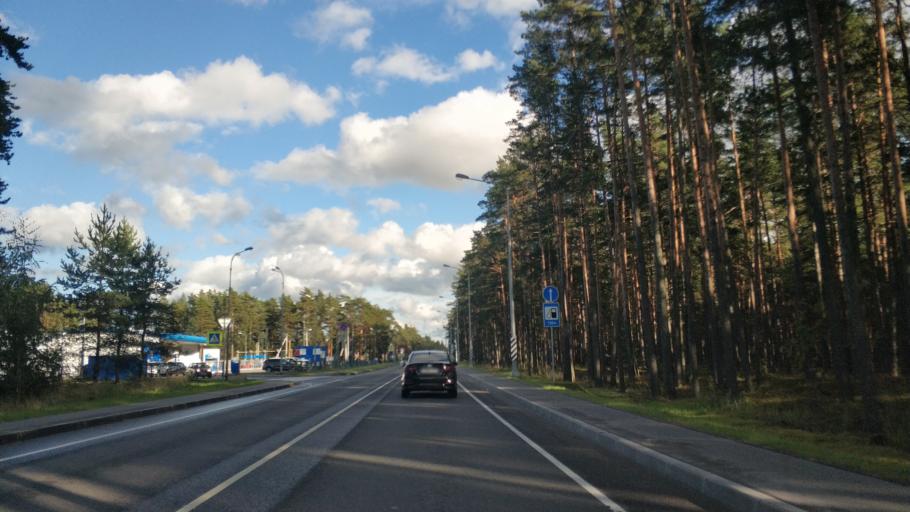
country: RU
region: Leningrad
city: Priozersk
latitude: 61.0161
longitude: 30.1441
